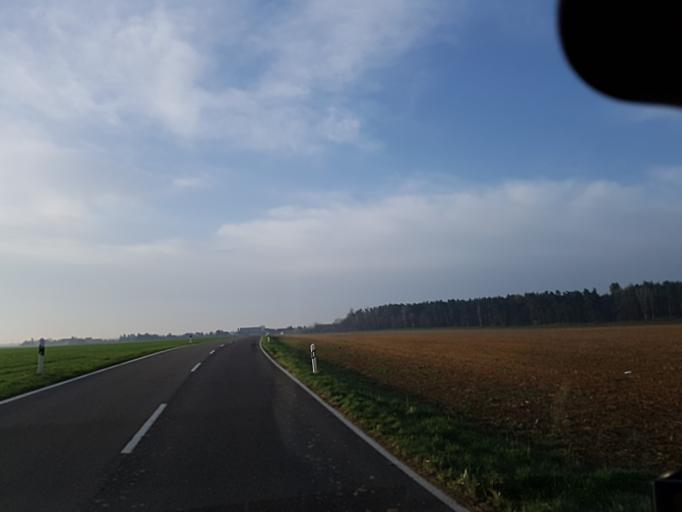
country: DE
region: Saxony
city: Strehla
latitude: 51.3870
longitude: 13.2781
